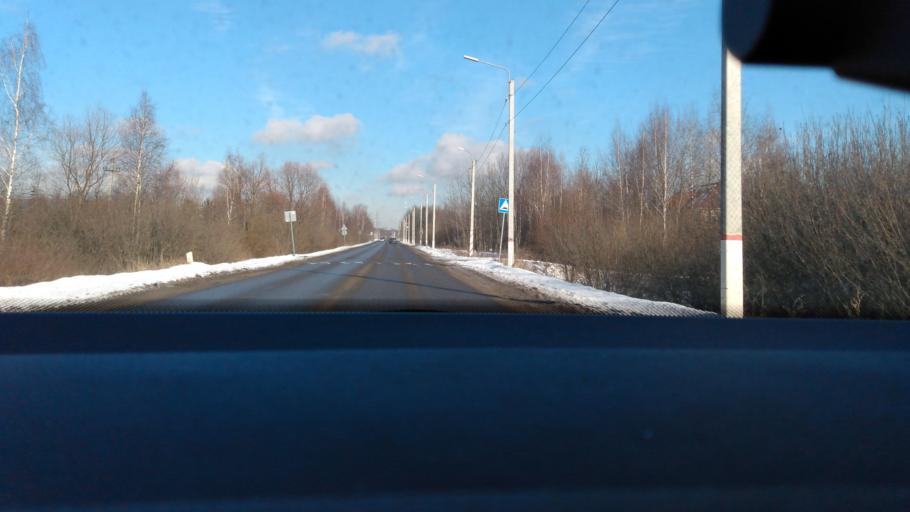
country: RU
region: Moskovskaya
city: Kratovo
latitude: 55.6260
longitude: 38.1583
